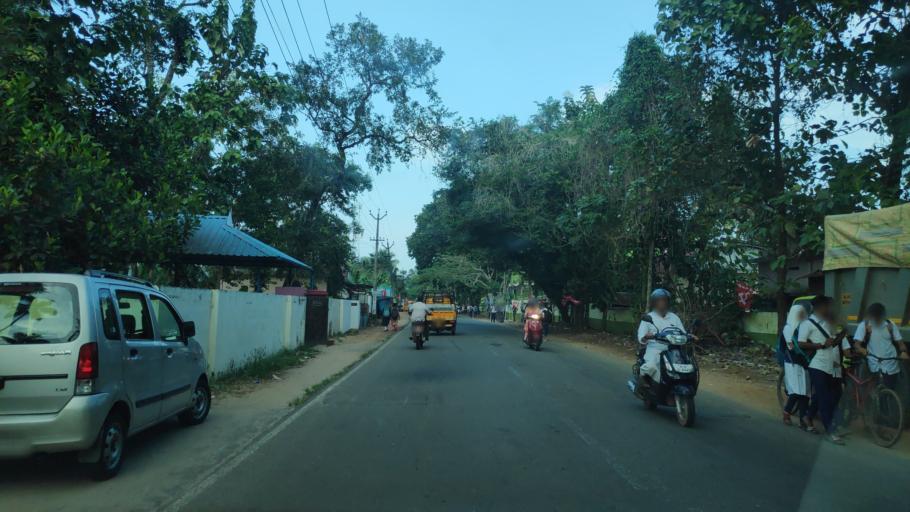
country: IN
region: Kerala
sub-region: Alappuzha
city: Alleppey
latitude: 9.5754
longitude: 76.3486
